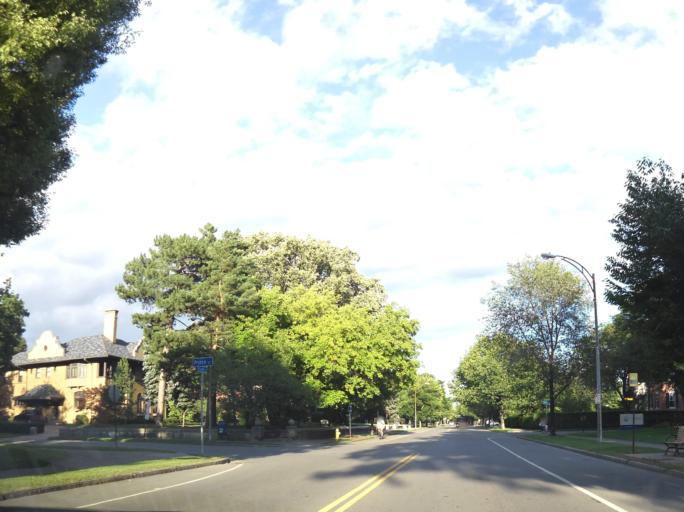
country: US
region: New York
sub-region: Monroe County
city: Rochester
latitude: 43.1546
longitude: -77.5928
